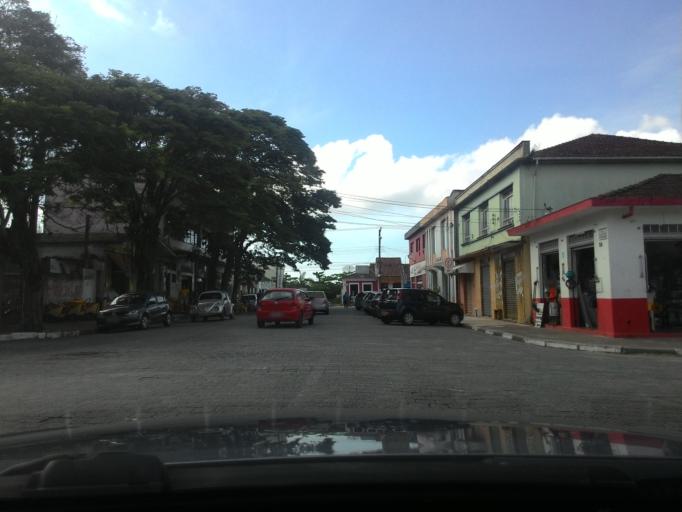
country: BR
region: Sao Paulo
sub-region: Iguape
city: Iguape
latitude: -24.7105
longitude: -47.5581
